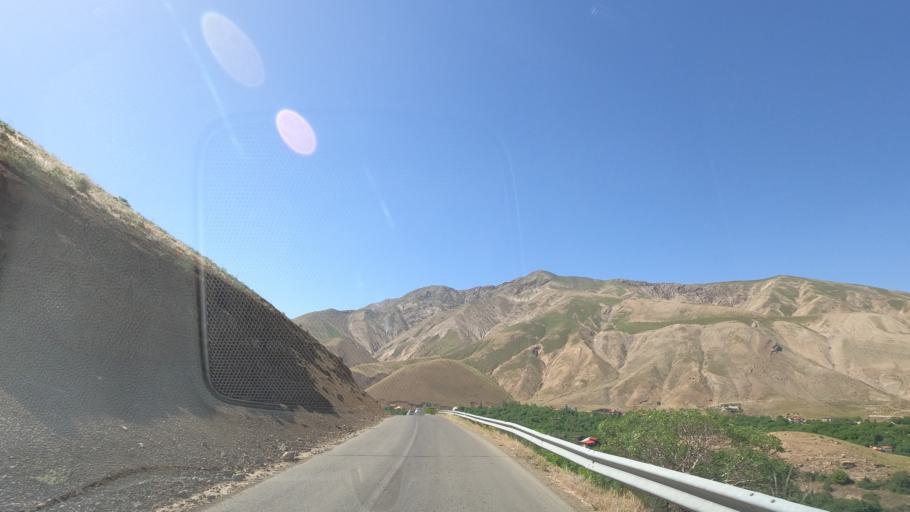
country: IR
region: Alborz
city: Karaj
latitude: 35.9278
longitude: 51.0872
